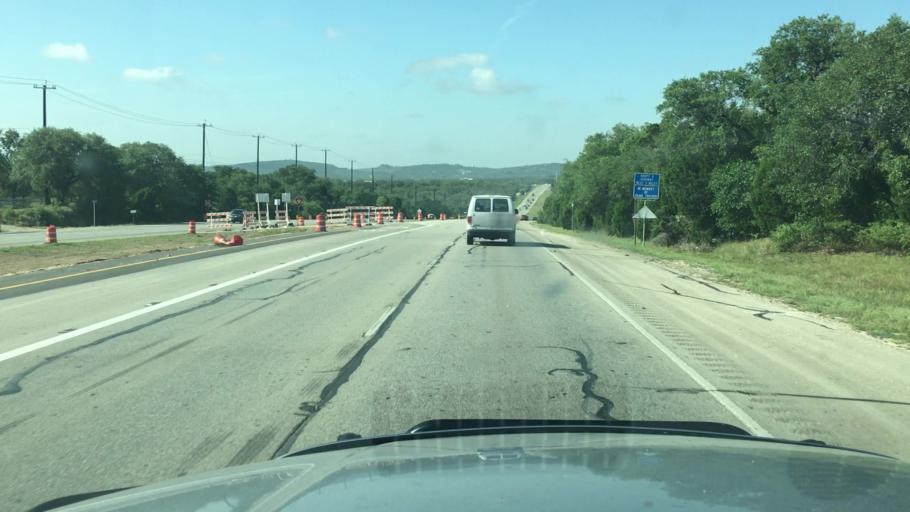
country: US
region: Texas
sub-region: Comal County
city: Bulverde
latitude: 29.7598
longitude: -98.4303
